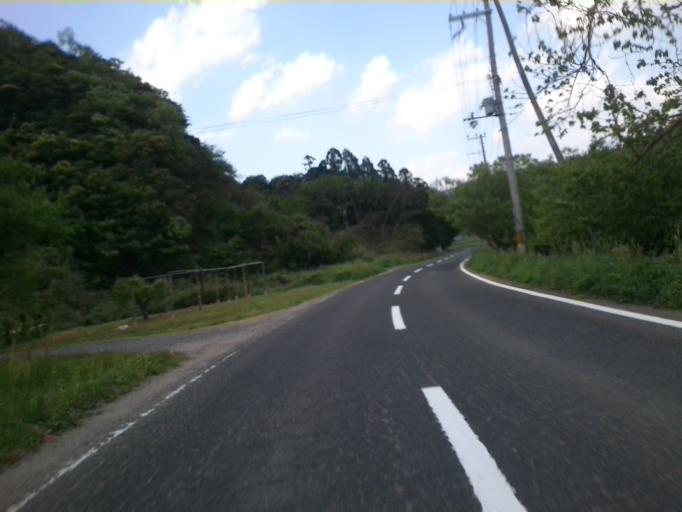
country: JP
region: Kyoto
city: Miyazu
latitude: 35.7007
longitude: 135.1018
